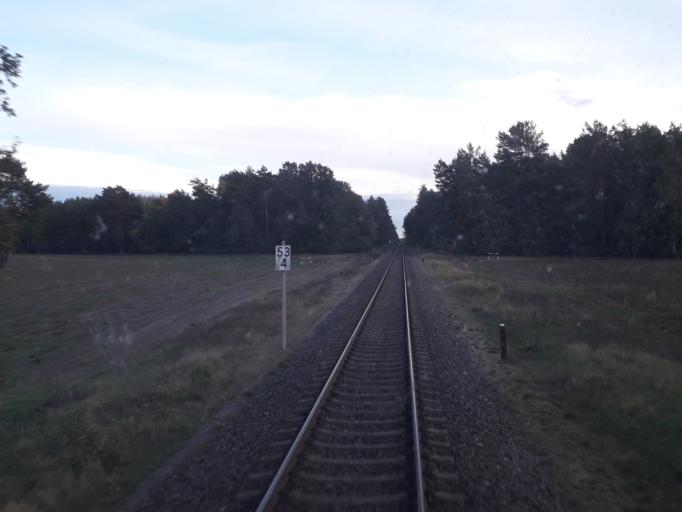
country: DE
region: Brandenburg
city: Wittstock
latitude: 53.0628
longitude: 12.5477
